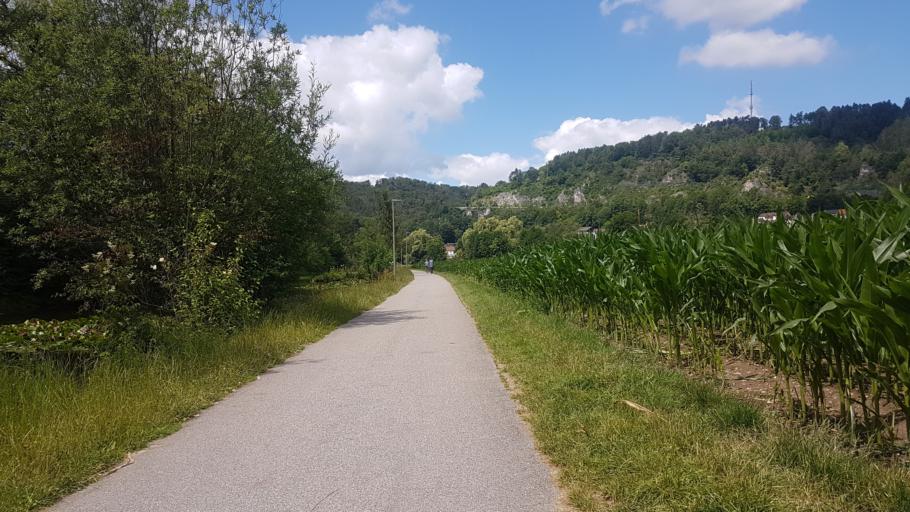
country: DE
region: Bavaria
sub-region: Upper Bavaria
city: Eichstaett
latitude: 48.8991
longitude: 11.1722
